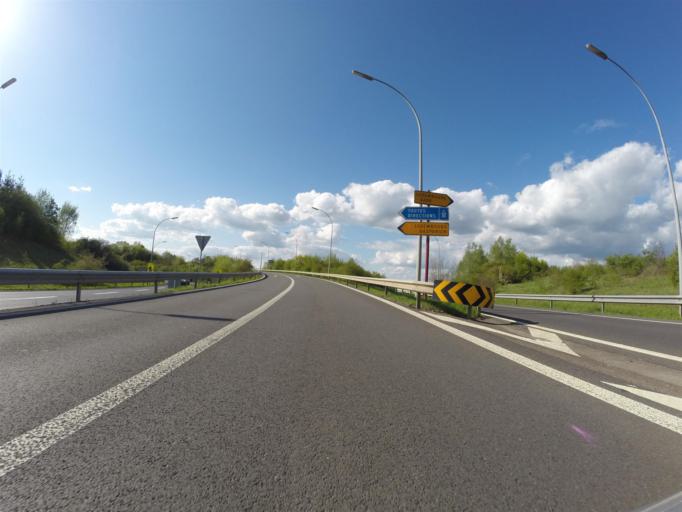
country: LU
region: Luxembourg
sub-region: Canton de Luxembourg
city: Hesperange
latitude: 49.5811
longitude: 6.1310
